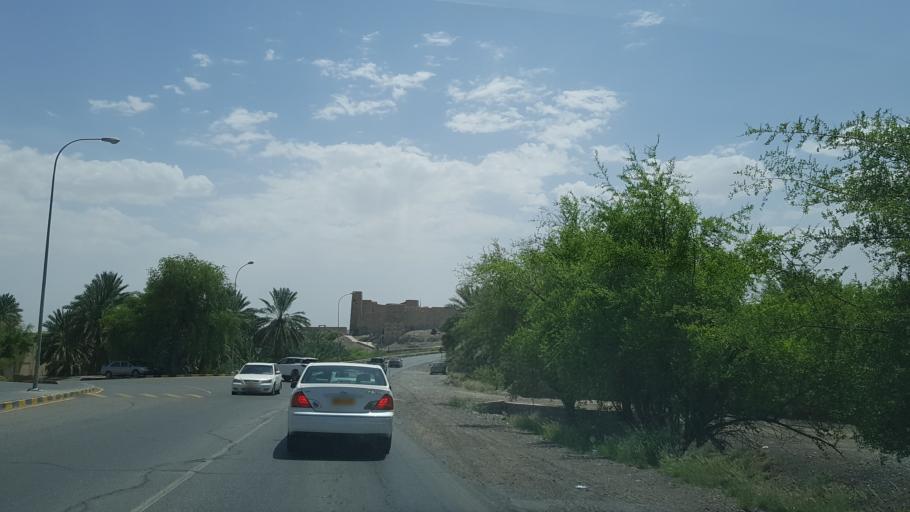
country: OM
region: Muhafazat ad Dakhiliyah
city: Bahla'
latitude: 22.9678
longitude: 57.3022
